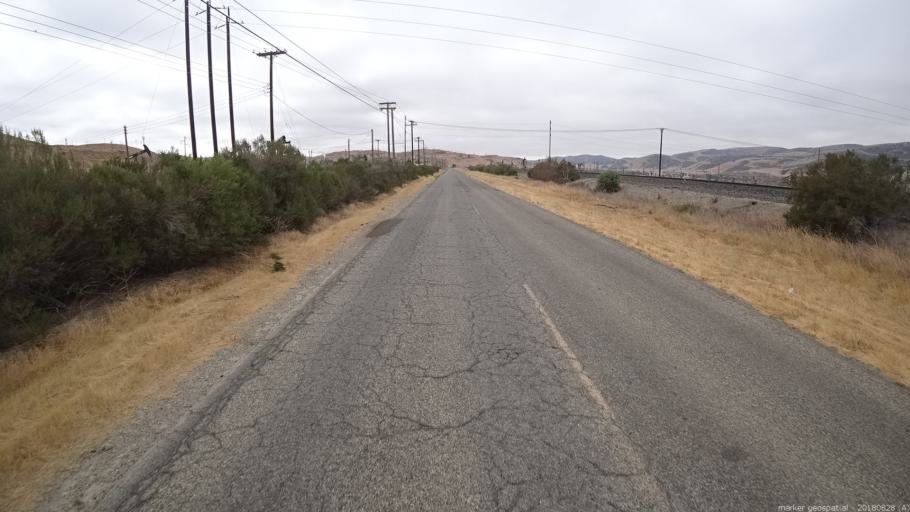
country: US
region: California
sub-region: San Luis Obispo County
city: Lake Nacimiento
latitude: 35.9592
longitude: -120.8662
